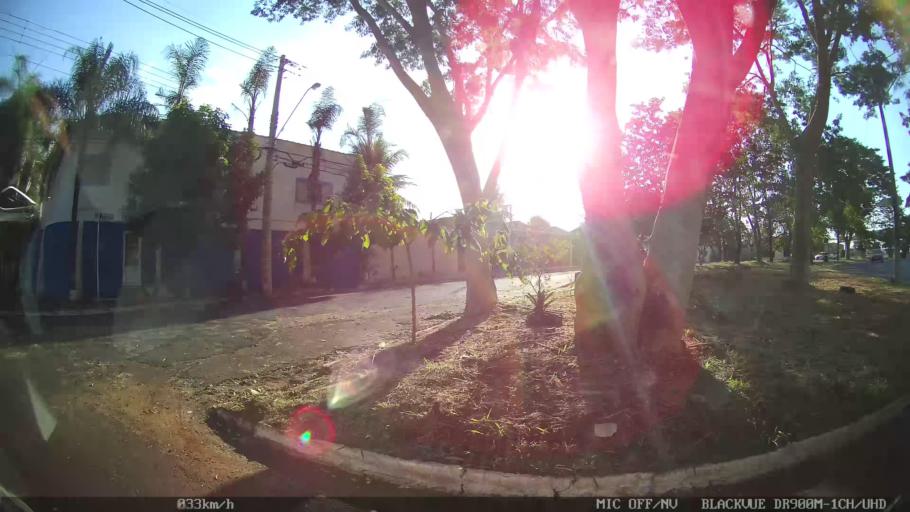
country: BR
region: Sao Paulo
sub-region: Ribeirao Preto
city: Ribeirao Preto
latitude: -21.1575
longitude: -47.8390
